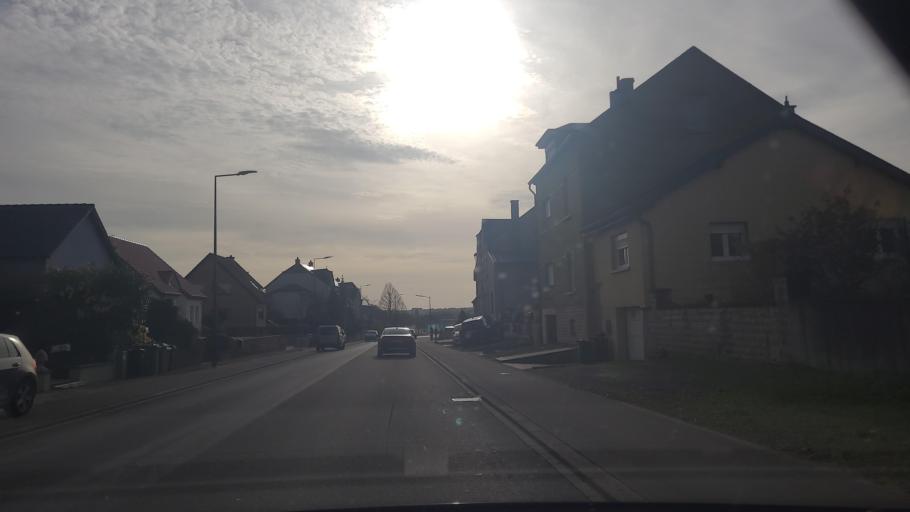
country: LU
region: Luxembourg
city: Hautcharage
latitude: 49.5799
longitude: 5.9105
